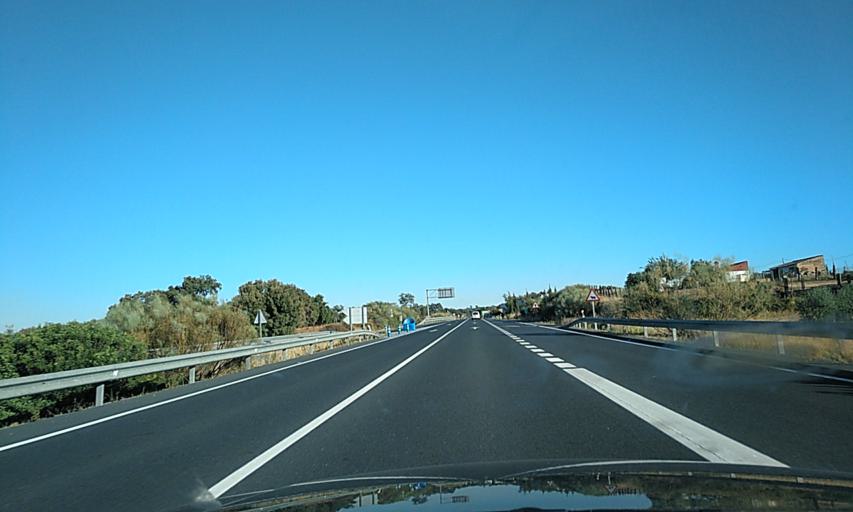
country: ES
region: Andalusia
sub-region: Provincia de Huelva
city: San Bartolome de la Torre
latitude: 37.4457
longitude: -7.1243
